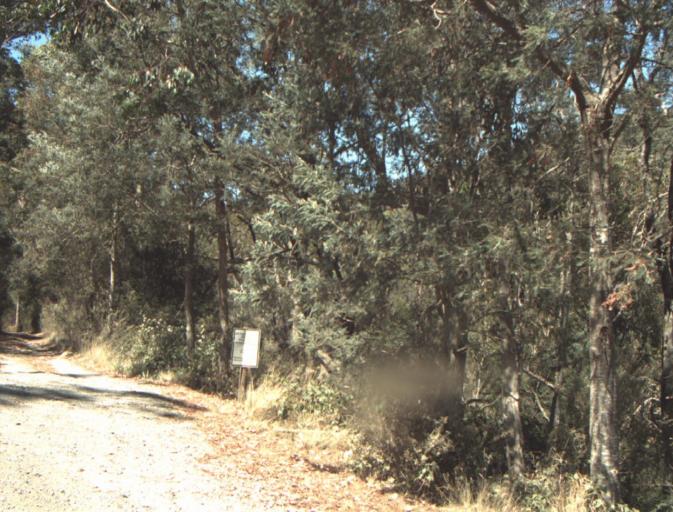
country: AU
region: Tasmania
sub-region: Dorset
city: Scottsdale
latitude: -41.2936
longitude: 147.4088
